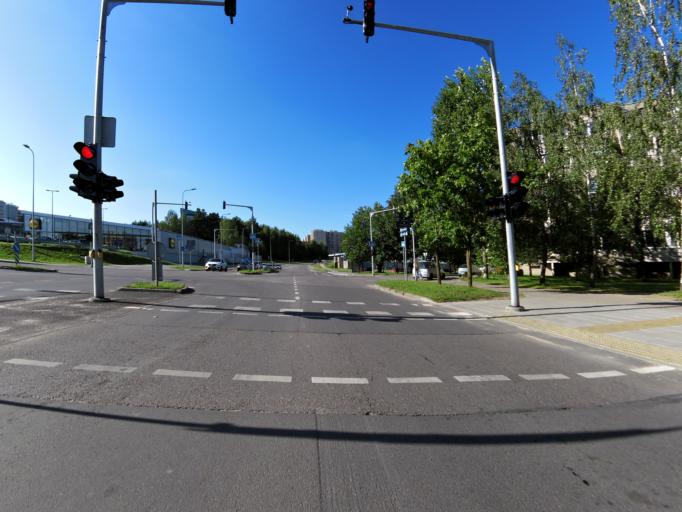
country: LT
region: Vilnius County
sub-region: Vilnius
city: Fabijoniskes
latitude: 54.7374
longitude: 25.2325
